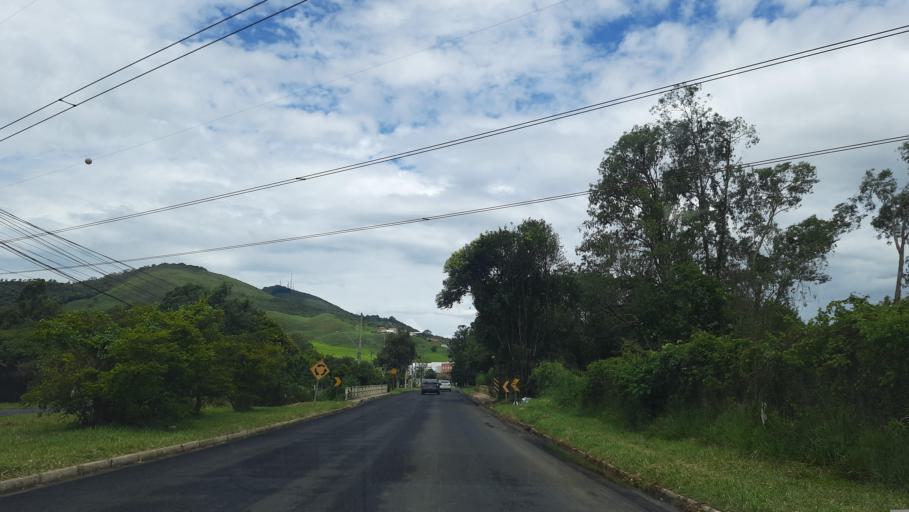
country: BR
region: Minas Gerais
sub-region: Pocos De Caldas
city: Pocos de Caldas
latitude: -21.7756
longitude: -46.6078
